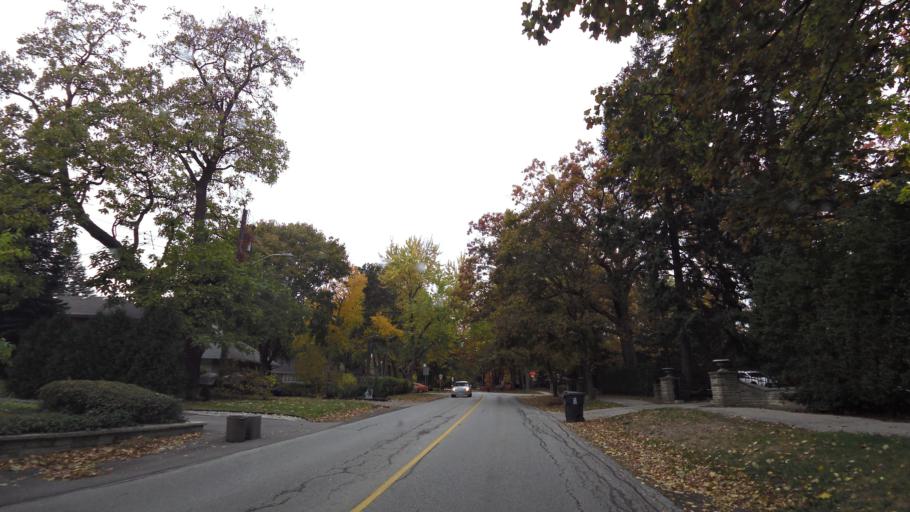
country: CA
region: Ontario
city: Etobicoke
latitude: 43.6667
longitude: -79.5272
